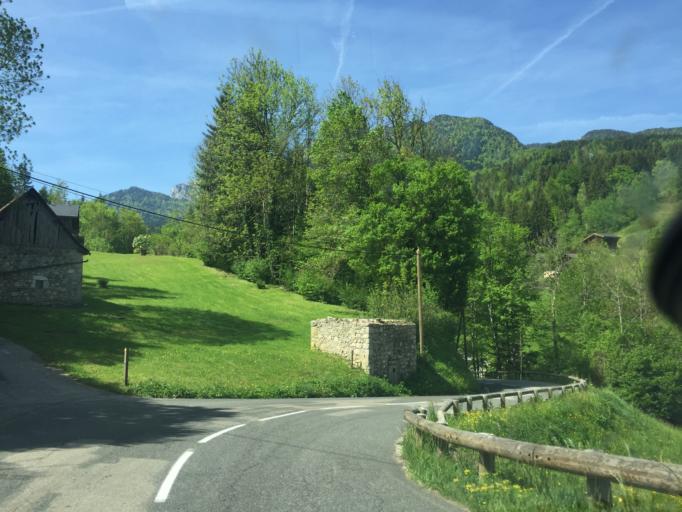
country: FR
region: Rhone-Alpes
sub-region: Departement de l'Isere
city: Saint-Vincent-de-Mercuze
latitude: 45.4126
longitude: 5.8549
